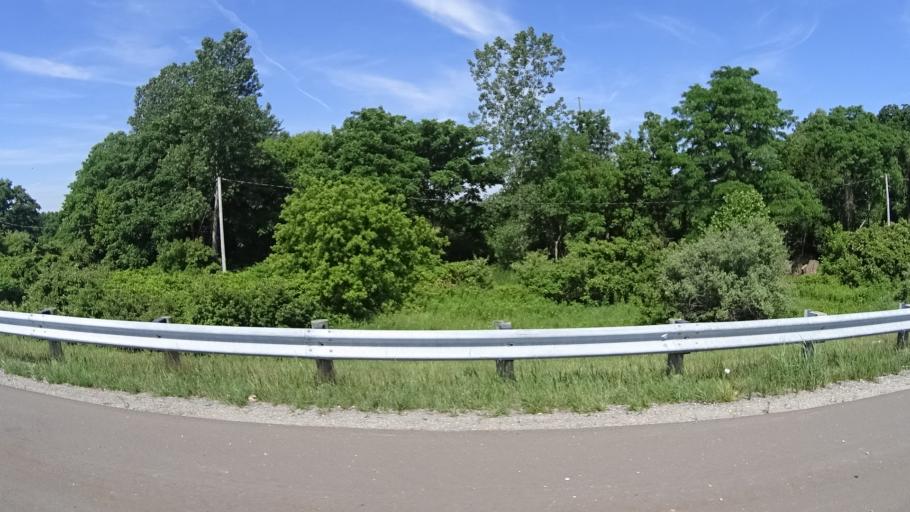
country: US
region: Ohio
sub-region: Erie County
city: Huron
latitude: 41.3697
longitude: -82.4941
